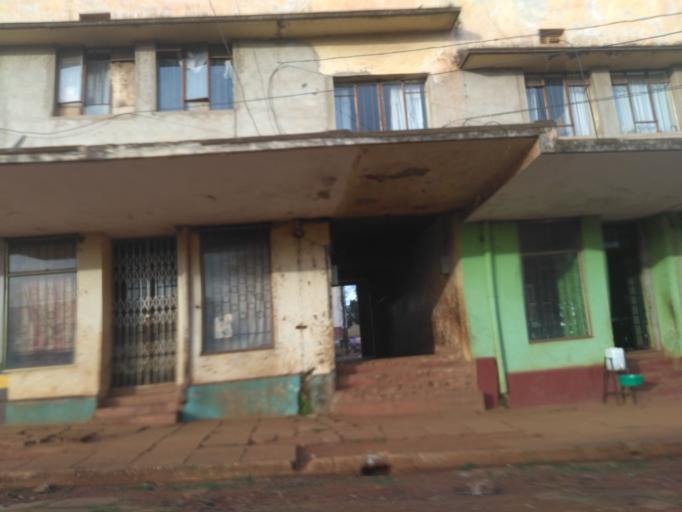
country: UG
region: Eastern Region
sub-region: Jinja District
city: Jinja
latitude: 0.4263
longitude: 33.2116
